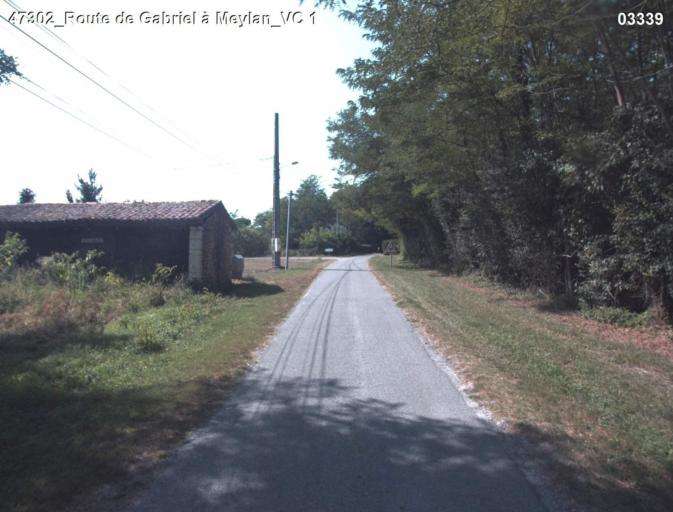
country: FR
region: Aquitaine
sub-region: Departement du Lot-et-Garonne
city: Mezin
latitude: 44.0736
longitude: 0.1233
